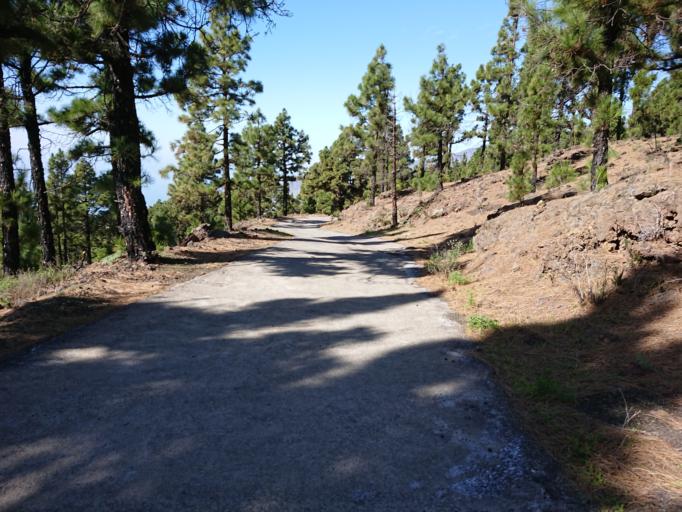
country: ES
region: Canary Islands
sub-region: Provincia de Santa Cruz de Tenerife
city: El Paso
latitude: 28.6074
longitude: -17.8650
